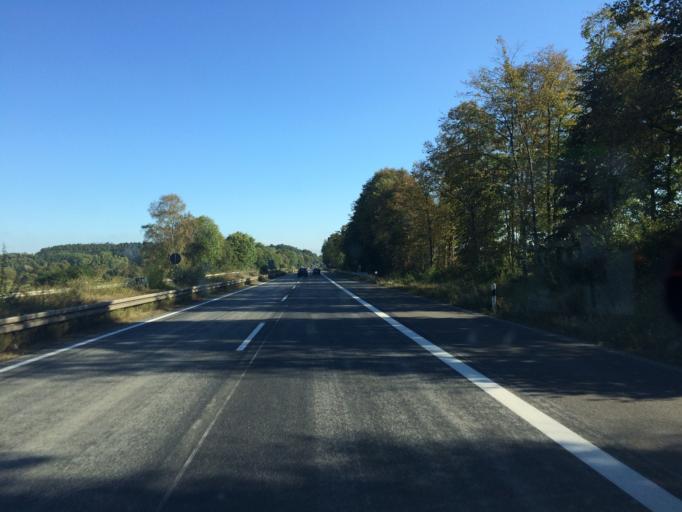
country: DE
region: Saarland
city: Bexbach
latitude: 49.3191
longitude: 7.2652
